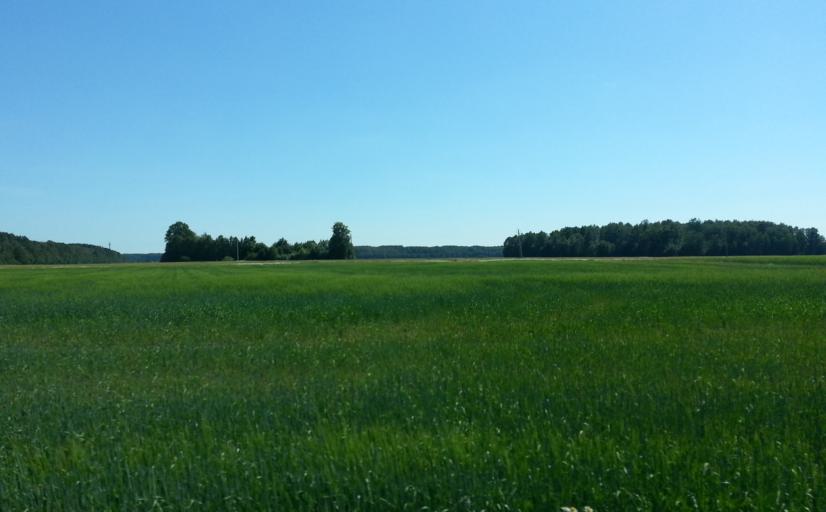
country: LT
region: Panevezys
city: Pasvalys
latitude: 56.2270
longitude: 24.4590
